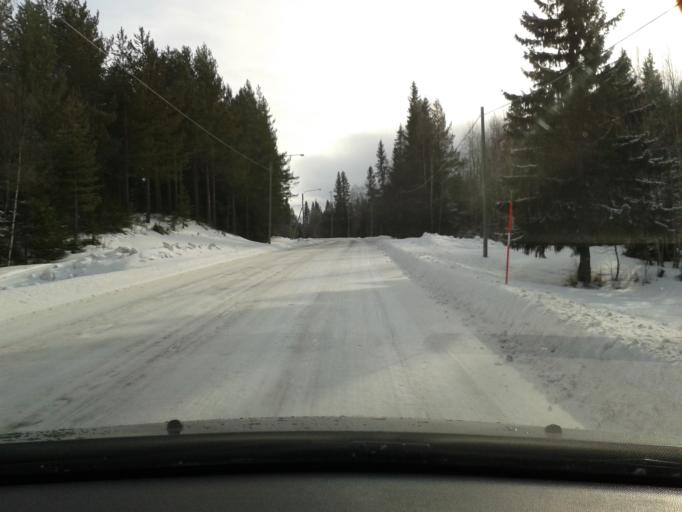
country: SE
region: Vaesterbotten
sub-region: Vilhelmina Kommun
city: Sjoberg
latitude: 64.6888
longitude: 16.2734
